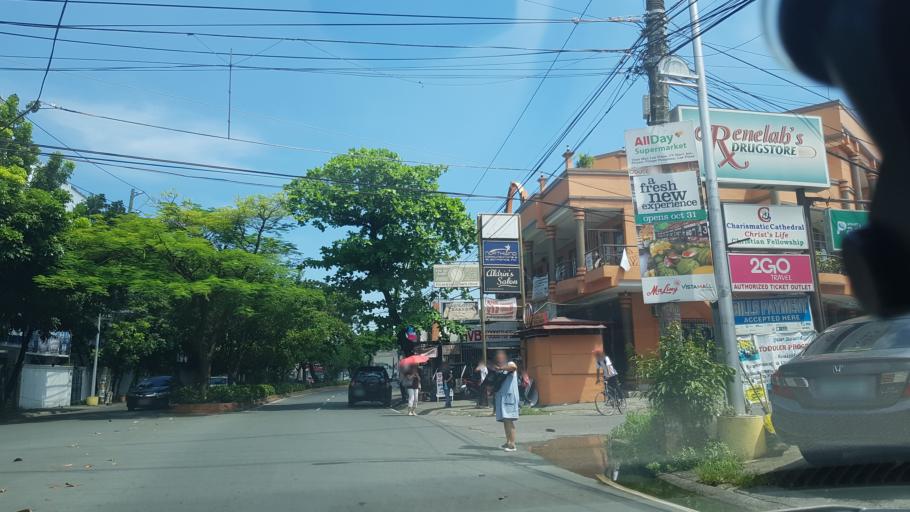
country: PH
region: Calabarzon
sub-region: Province of Rizal
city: Las Pinas
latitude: 14.4403
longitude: 120.9912
